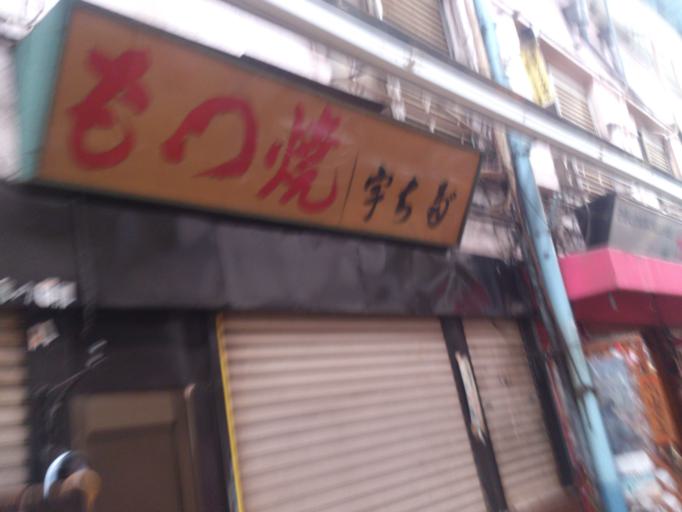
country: JP
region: Chiba
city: Matsudo
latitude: 35.7382
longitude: 139.8489
